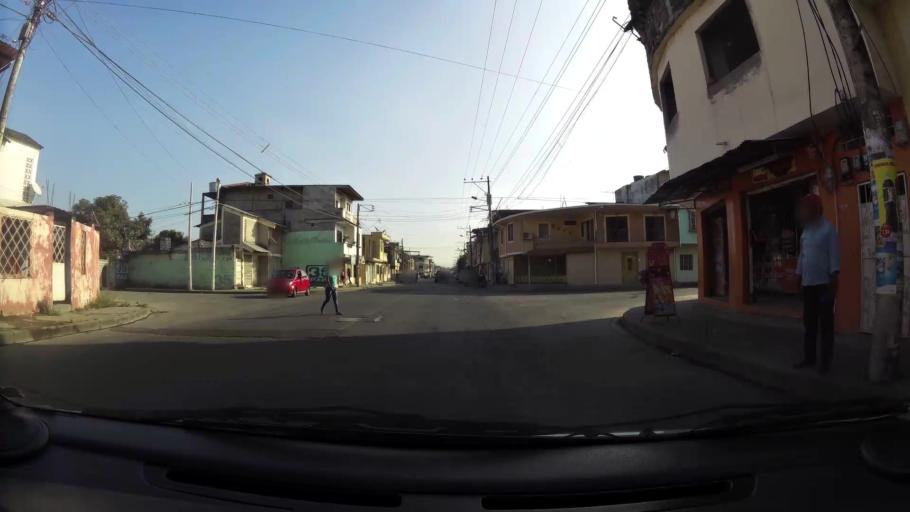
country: EC
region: Guayas
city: Eloy Alfaro
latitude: -2.1837
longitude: -79.8562
